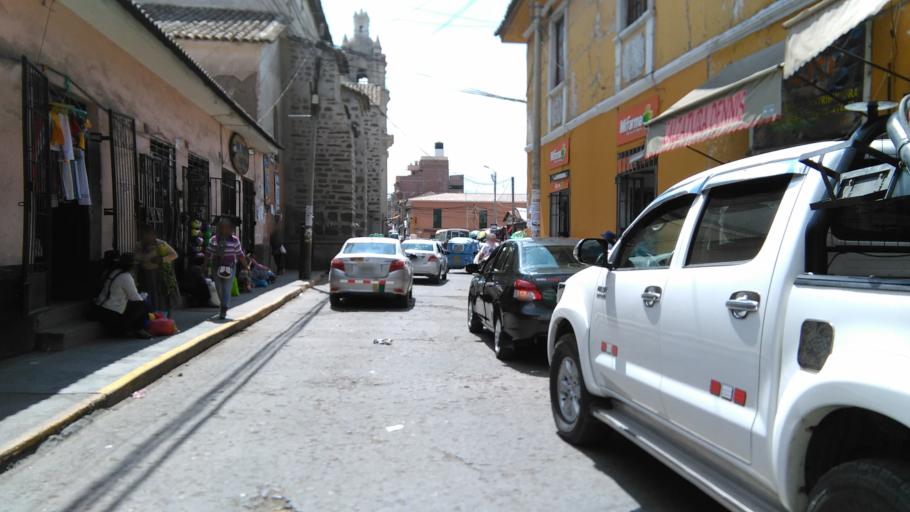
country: PE
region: Ayacucho
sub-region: Provincia de Huamanga
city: Ayacucho
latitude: -13.1638
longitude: -74.2284
